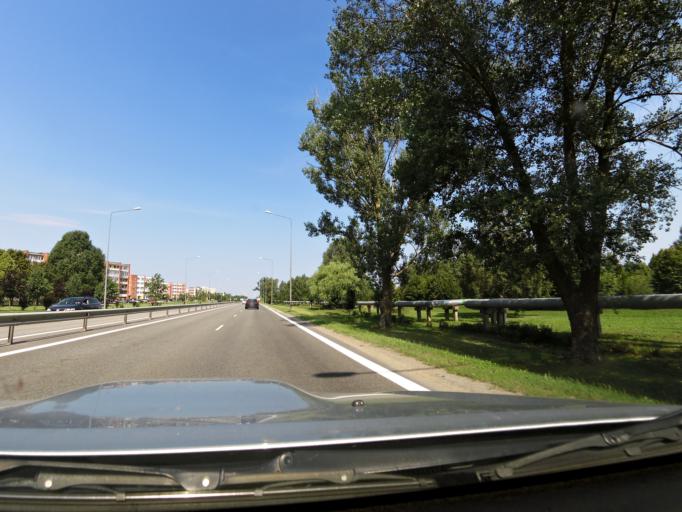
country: LT
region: Siauliu apskritis
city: Radviliskis
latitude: 55.8181
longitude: 23.5378
